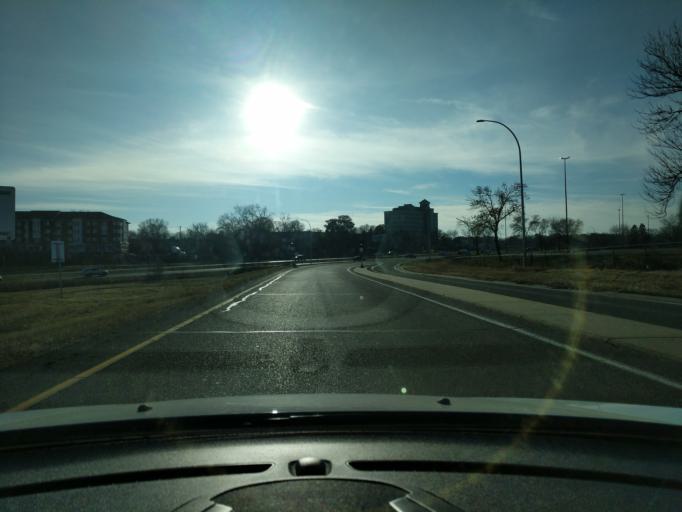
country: US
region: Minnesota
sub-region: Ramsey County
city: Roseville
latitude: 45.0113
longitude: -93.1679
